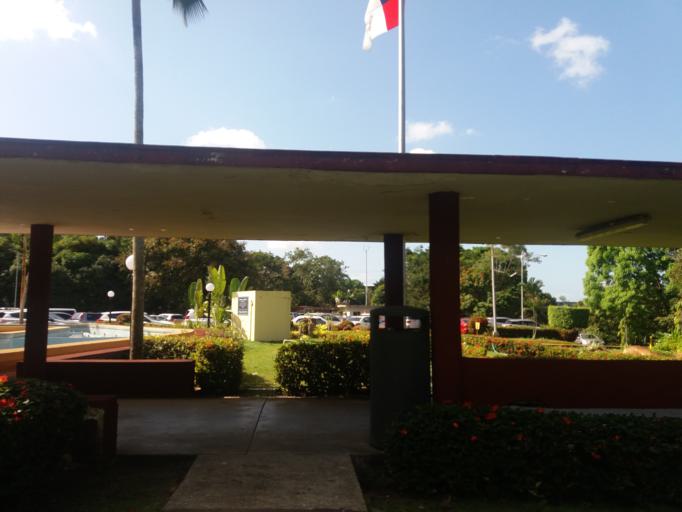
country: PA
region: Panama
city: Panama
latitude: 8.9835
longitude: -79.5335
